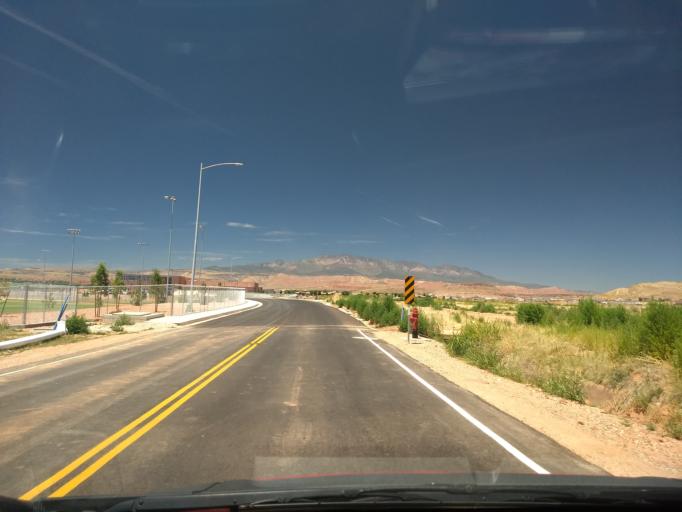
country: US
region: Utah
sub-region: Washington County
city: Washington
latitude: 37.0686
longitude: -113.5061
